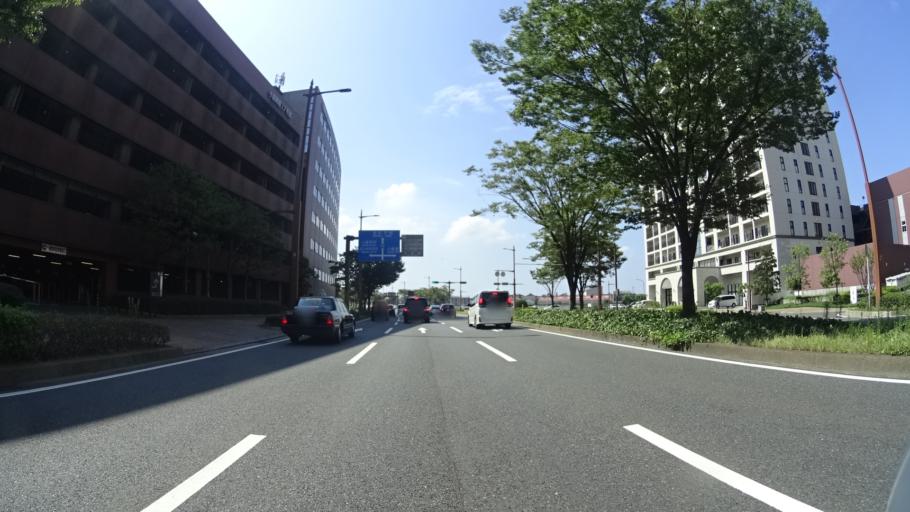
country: JP
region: Fukuoka
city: Kitakyushu
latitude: 33.8896
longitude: 130.8821
